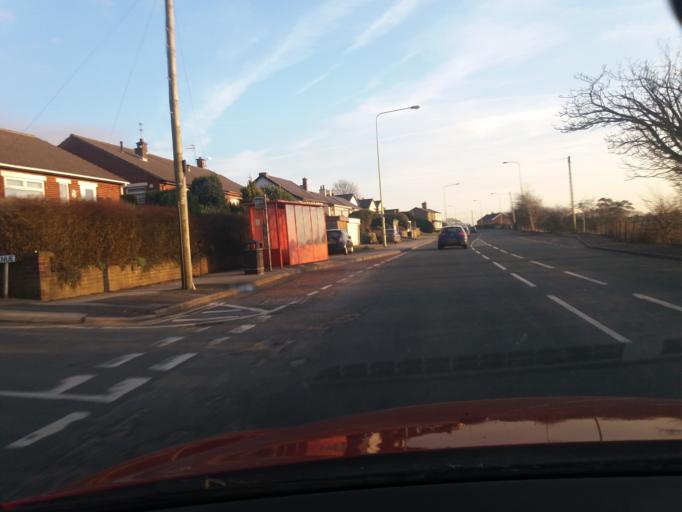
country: GB
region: England
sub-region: Lancashire
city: Chorley
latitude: 53.6725
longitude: -2.6160
